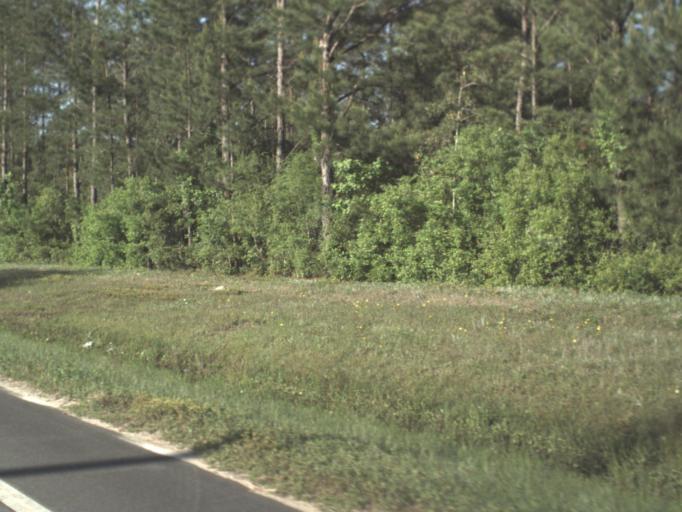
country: US
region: Florida
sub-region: Liberty County
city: Bristol
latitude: 30.3612
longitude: -84.8179
